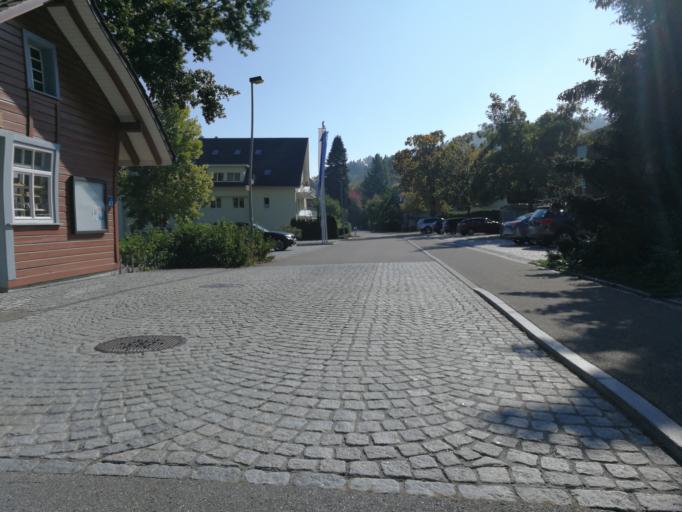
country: CH
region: Zurich
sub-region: Bezirk Uster
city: Egg
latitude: 47.2995
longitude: 8.6871
